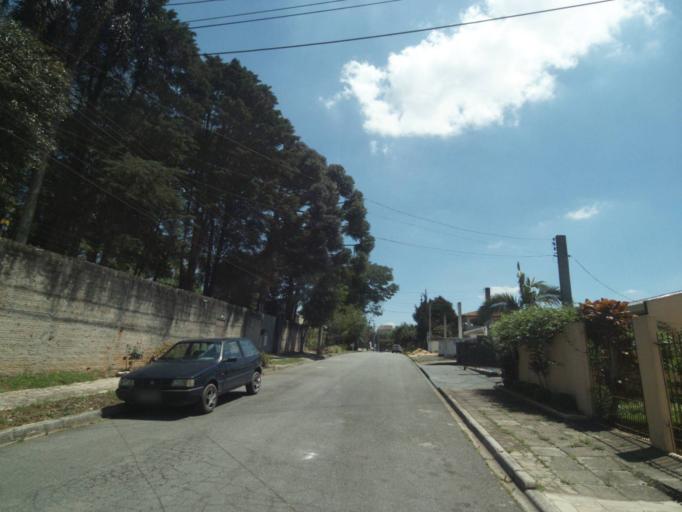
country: BR
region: Parana
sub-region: Curitiba
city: Curitiba
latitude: -25.3953
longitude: -49.2276
